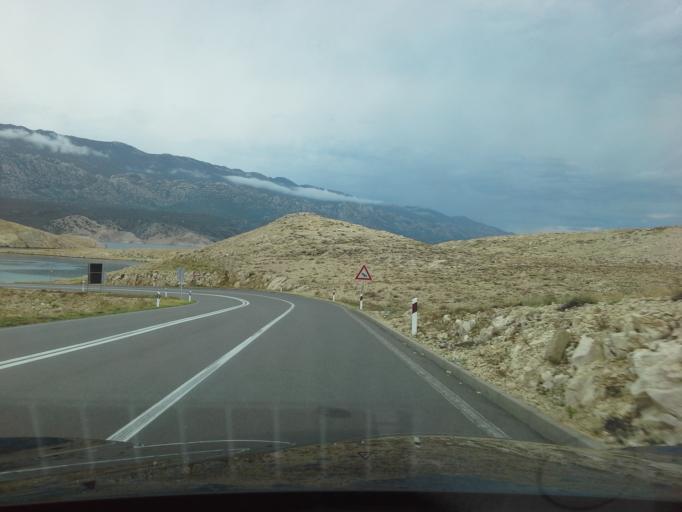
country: HR
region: Primorsko-Goranska
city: Banjol
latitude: 44.7052
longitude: 14.8568
